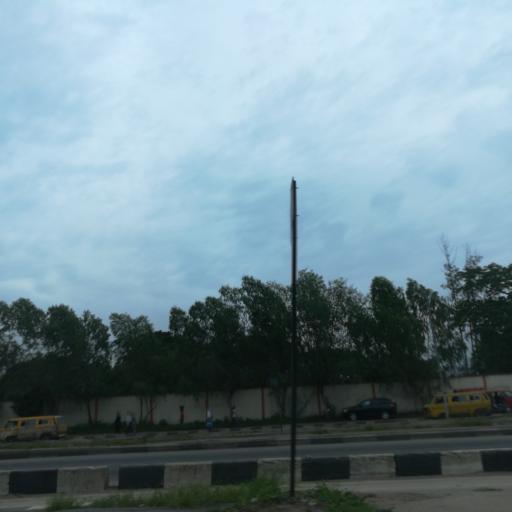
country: NG
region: Lagos
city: Ojota
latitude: 6.5676
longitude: 3.3670
